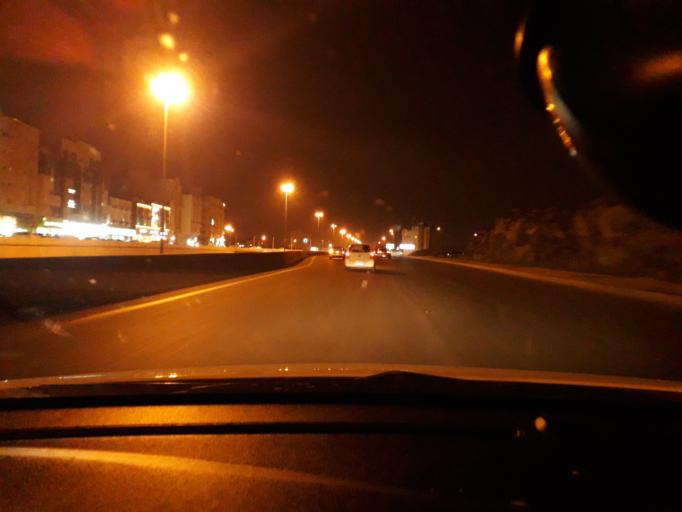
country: SA
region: Al Madinah al Munawwarah
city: Medina
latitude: 24.4564
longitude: 39.5883
